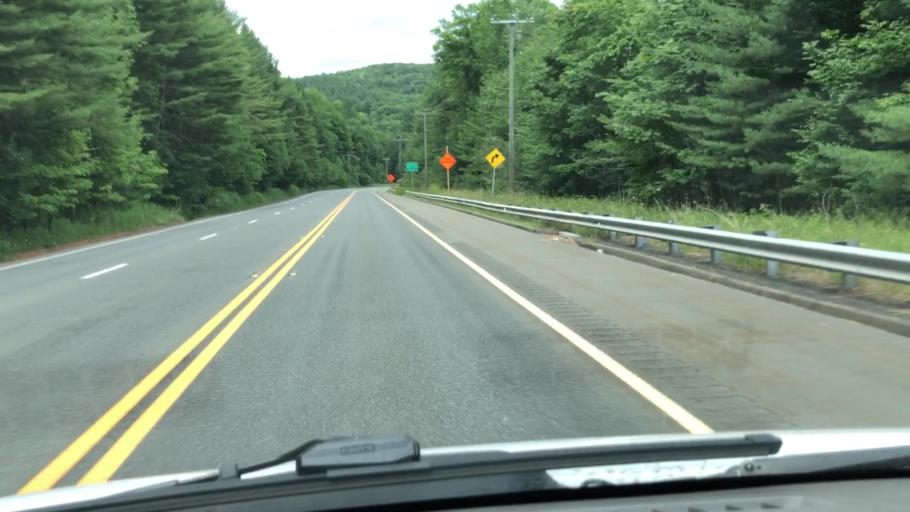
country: US
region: Massachusetts
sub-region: Berkshire County
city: Hinsdale
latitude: 42.4873
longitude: -72.9791
